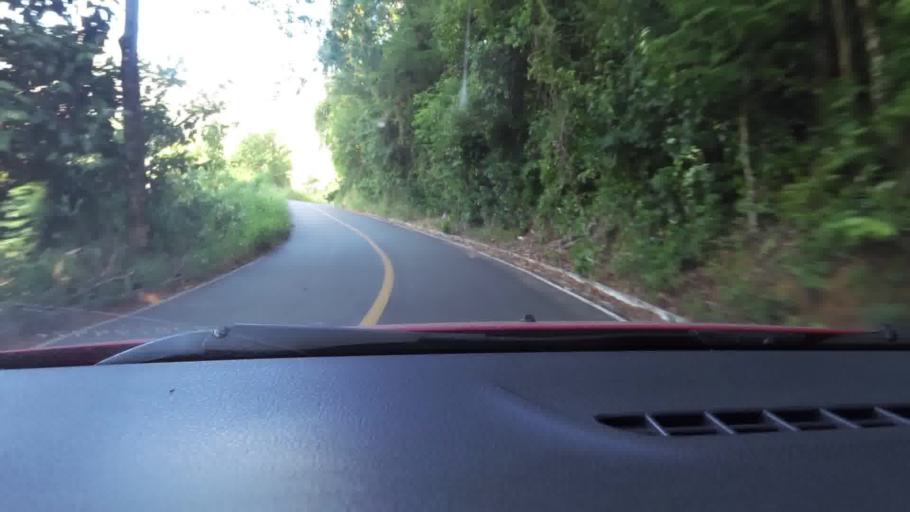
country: BR
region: Espirito Santo
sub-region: Guarapari
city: Guarapari
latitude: -20.5766
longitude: -40.5422
